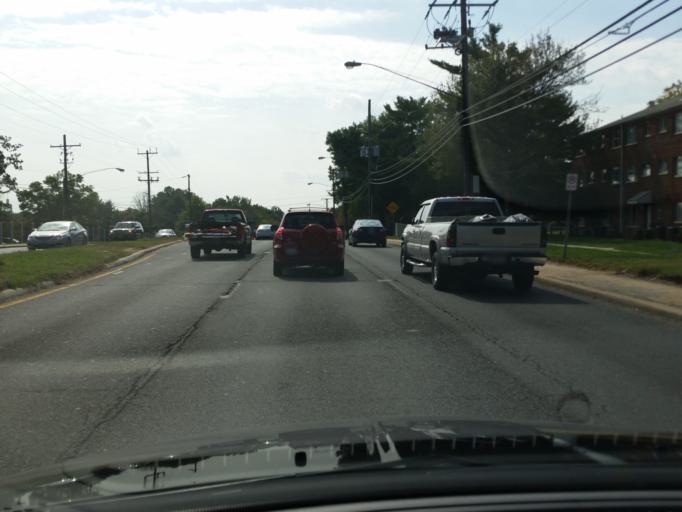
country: US
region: Maryland
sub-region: Prince George's County
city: Adelphi
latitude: 39.0058
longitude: -76.9807
